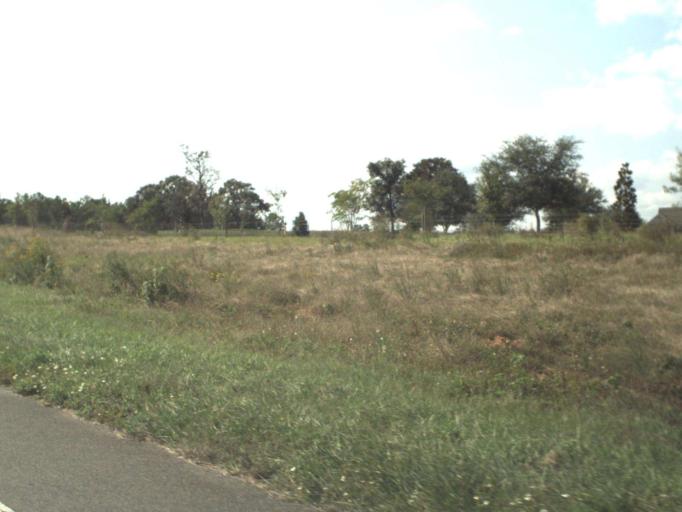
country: US
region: Florida
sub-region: Holmes County
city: Bonifay
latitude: 30.5937
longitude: -85.7820
